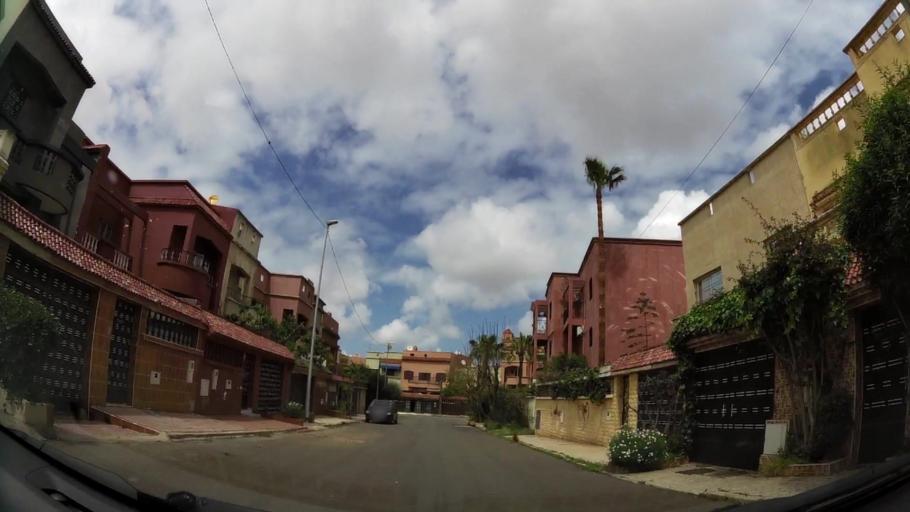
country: MA
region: Grand Casablanca
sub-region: Casablanca
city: Casablanca
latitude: 33.5320
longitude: -7.6036
